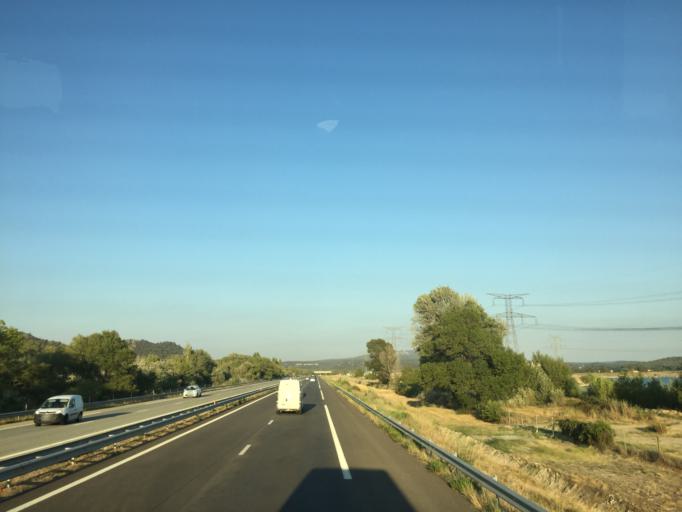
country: FR
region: Provence-Alpes-Cote d'Azur
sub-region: Departement des Bouches-du-Rhone
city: Peyrolles-en-Provence
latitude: 43.6586
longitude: 5.5629
